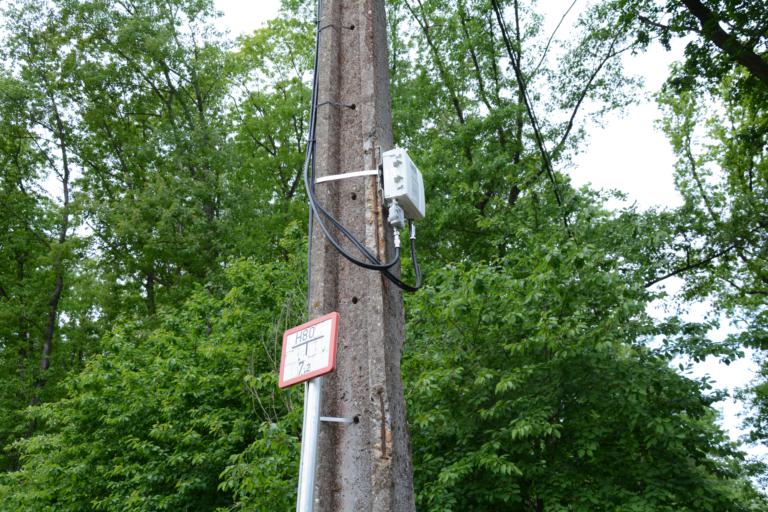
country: BE
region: Flanders
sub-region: Provincie Vlaams-Brabant
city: Boutersem
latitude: 50.8563
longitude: 4.8434
